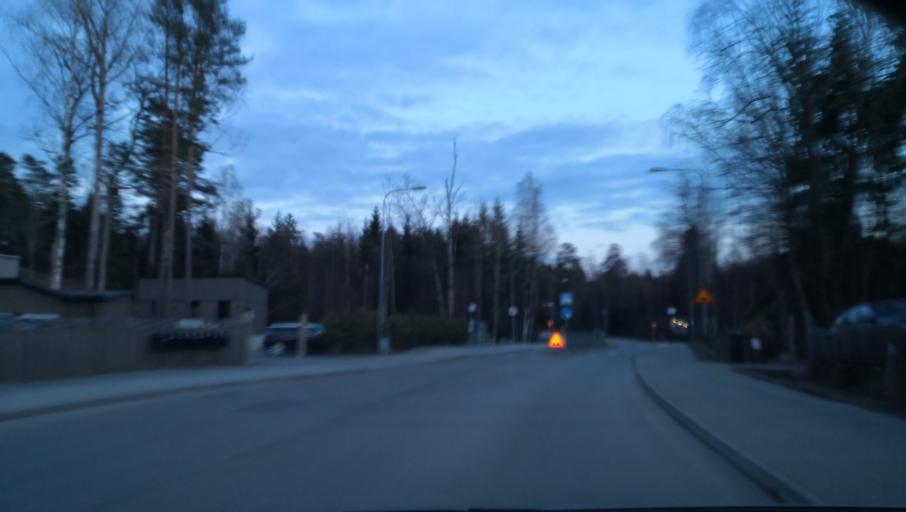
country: SE
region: Stockholm
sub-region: Nacka Kommun
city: Kummelnas
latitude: 59.3432
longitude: 18.2917
